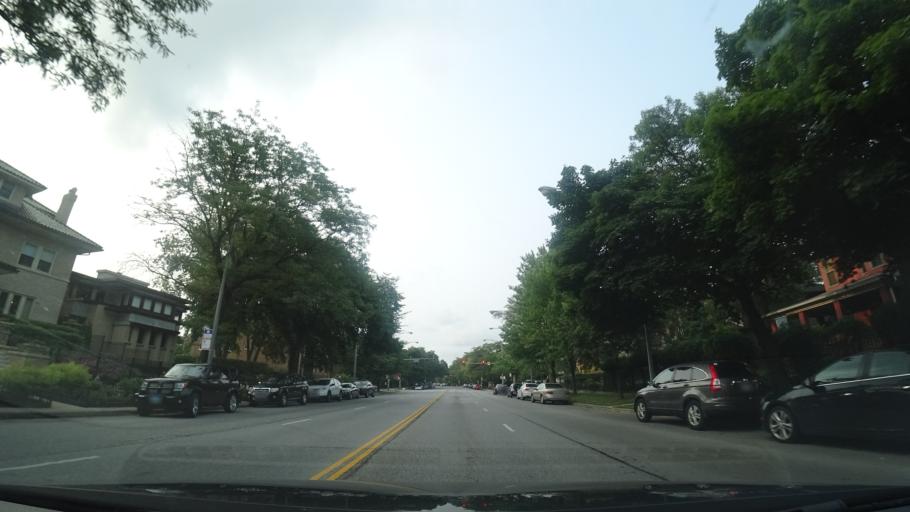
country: US
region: Illinois
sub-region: Cook County
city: Evanston
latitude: 42.0168
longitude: -87.6653
